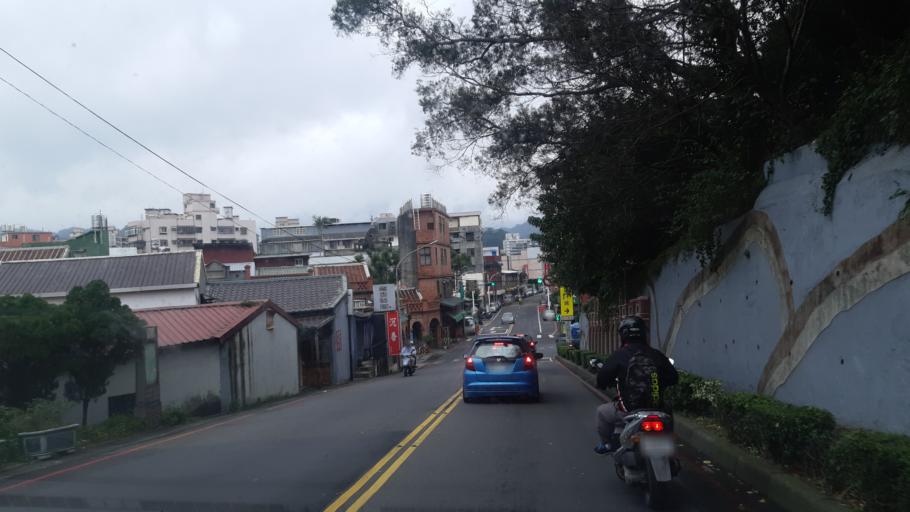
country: TW
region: Taiwan
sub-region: Taoyuan
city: Taoyuan
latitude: 24.9322
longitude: 121.3683
